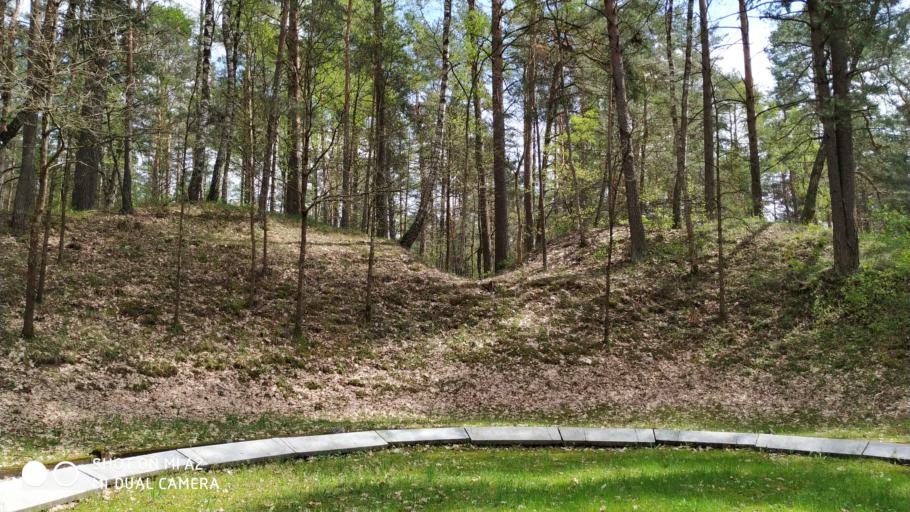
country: LT
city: Baltoji Voke
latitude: 54.6255
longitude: 25.1628
